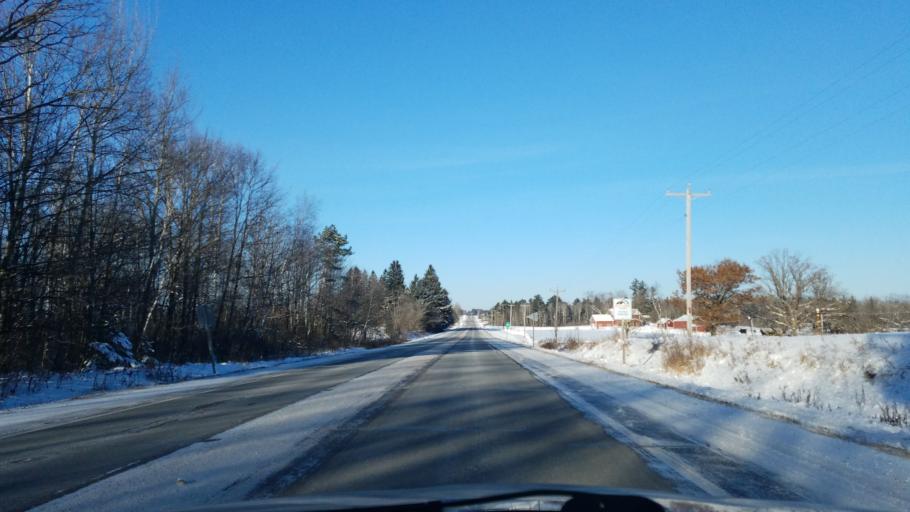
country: US
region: Wisconsin
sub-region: Barron County
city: Cumberland
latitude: 45.5053
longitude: -92.0524
